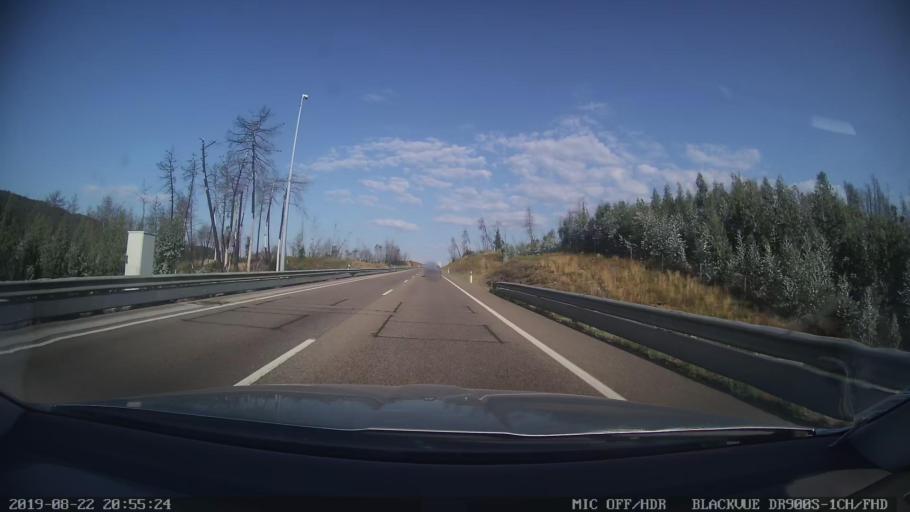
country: PT
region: Castelo Branco
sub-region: Serta
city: Serta
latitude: 39.7799
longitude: -8.0328
